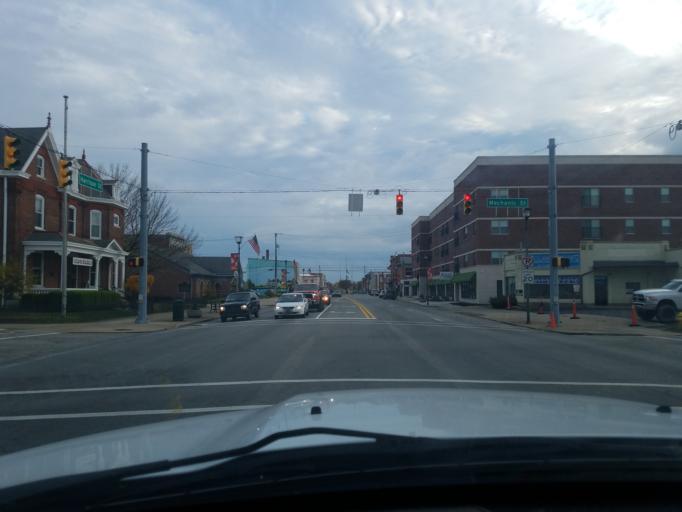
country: US
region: Indiana
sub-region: Shelby County
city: Shelbyville
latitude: 39.5263
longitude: -85.7770
